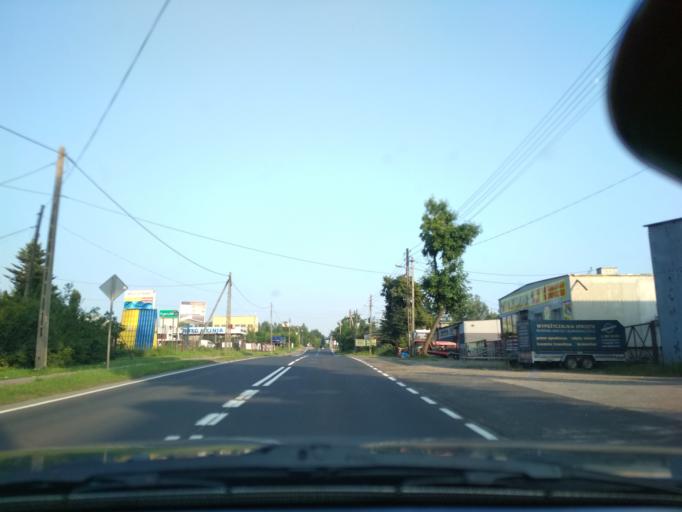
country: PL
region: Silesian Voivodeship
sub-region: Powiat zawiercianski
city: Ogrodzieniec
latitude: 50.4666
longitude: 19.4886
